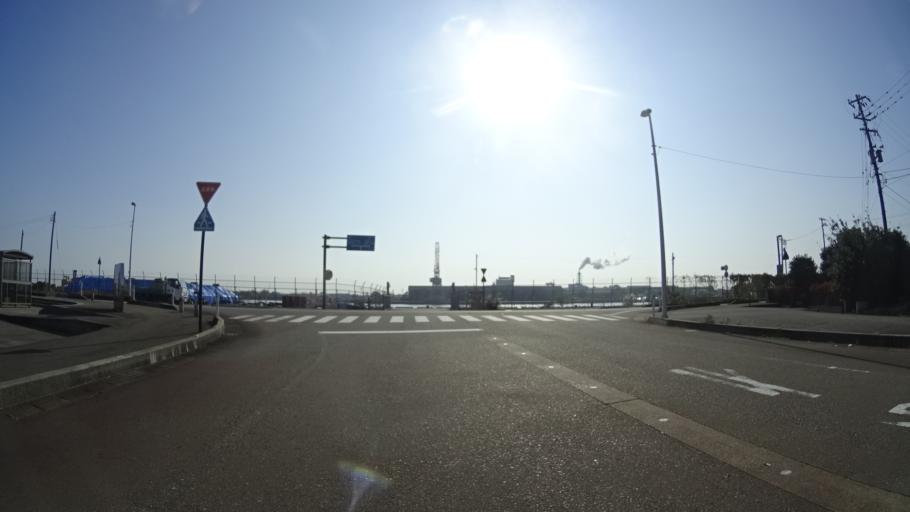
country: JP
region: Toyama
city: Nishishinminato
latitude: 36.7939
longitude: 137.0623
